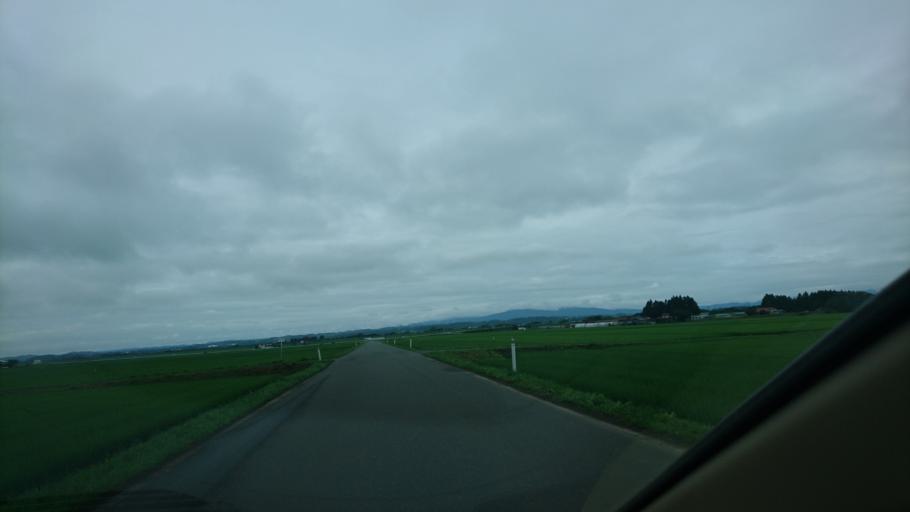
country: JP
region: Iwate
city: Mizusawa
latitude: 39.0643
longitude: 141.1770
